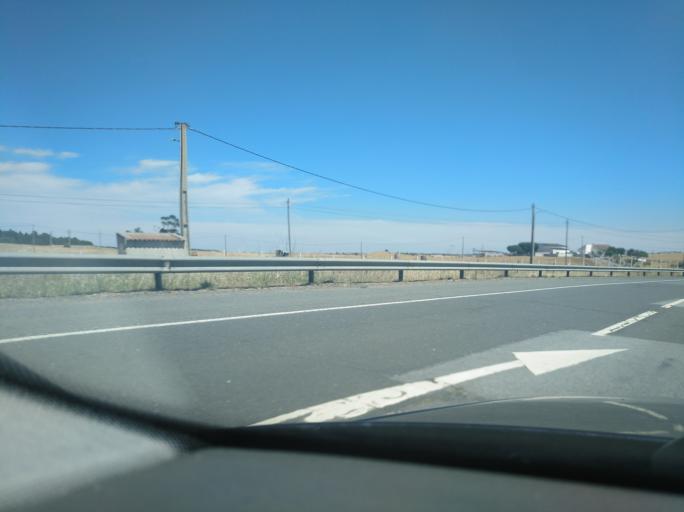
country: PT
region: Beja
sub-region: Castro Verde
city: Castro Verde
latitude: 37.6882
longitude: -8.0848
